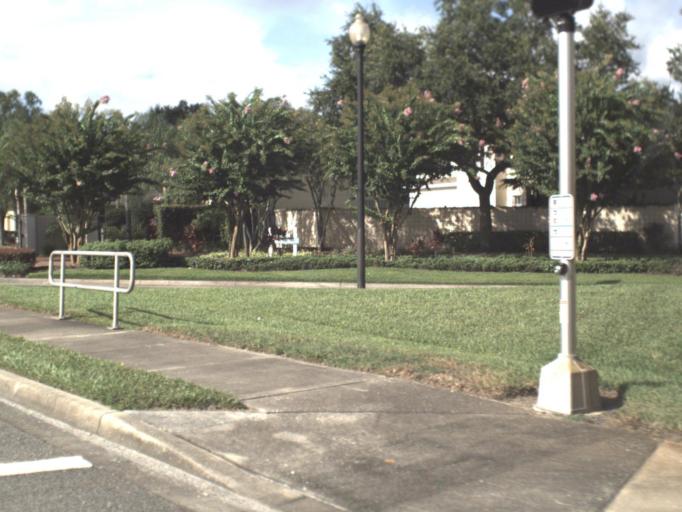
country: US
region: Florida
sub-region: Pasco County
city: Land O' Lakes
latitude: 28.2420
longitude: -82.4607
